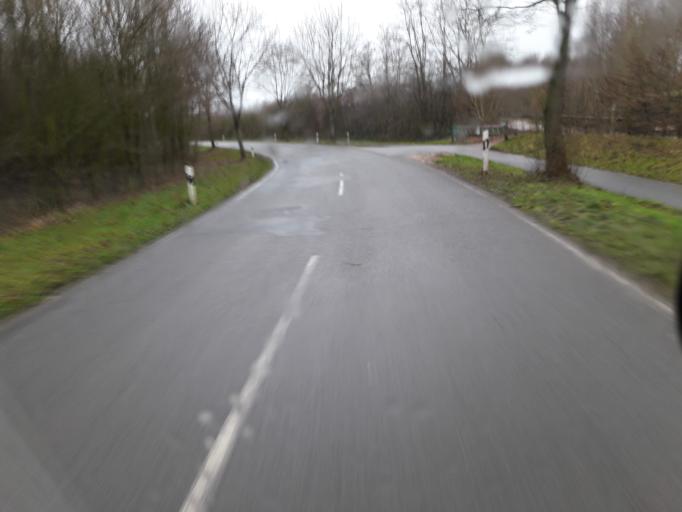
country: DE
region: Lower Saxony
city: Raddestorf
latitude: 52.4251
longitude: 8.9849
